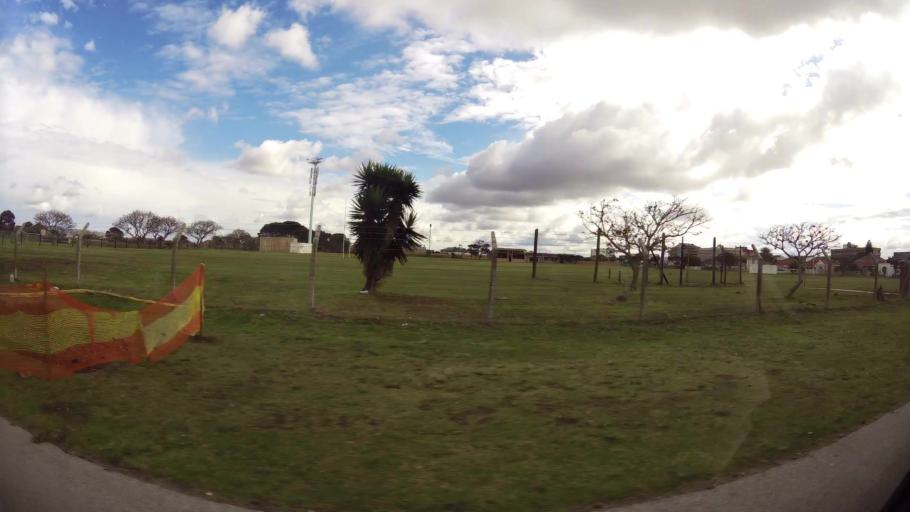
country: ZA
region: Eastern Cape
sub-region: Nelson Mandela Bay Metropolitan Municipality
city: Port Elizabeth
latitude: -33.9550
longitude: 25.5795
